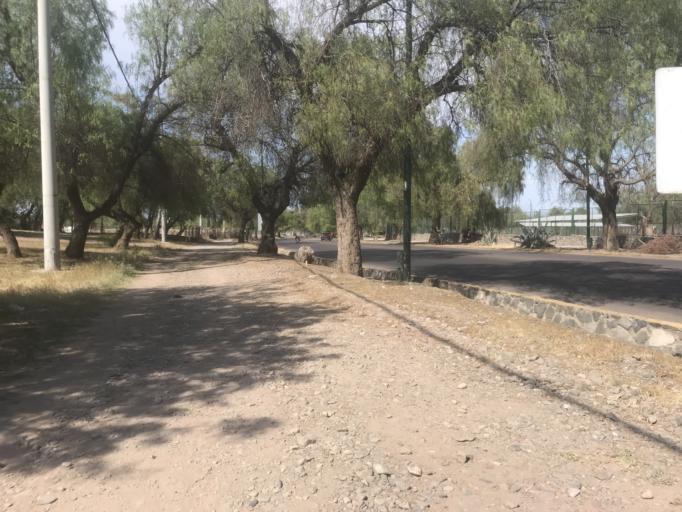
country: AR
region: Mendoza
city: Mendoza
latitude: -32.8837
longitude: -68.8888
